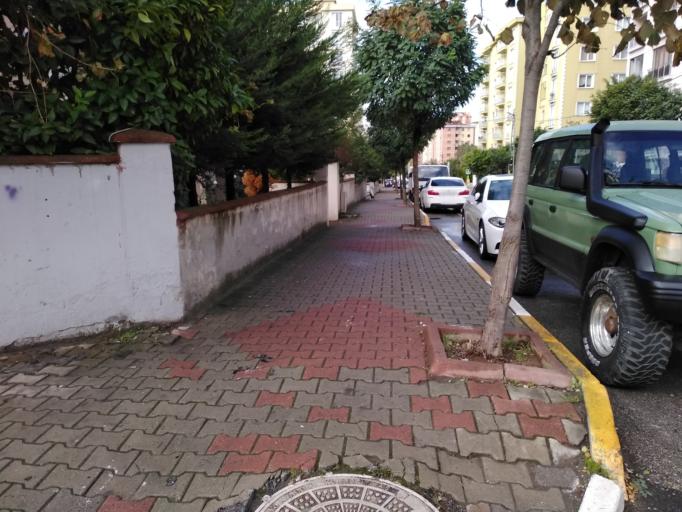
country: TR
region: Istanbul
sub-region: Atasehir
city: Atasehir
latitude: 40.9806
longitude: 29.1265
